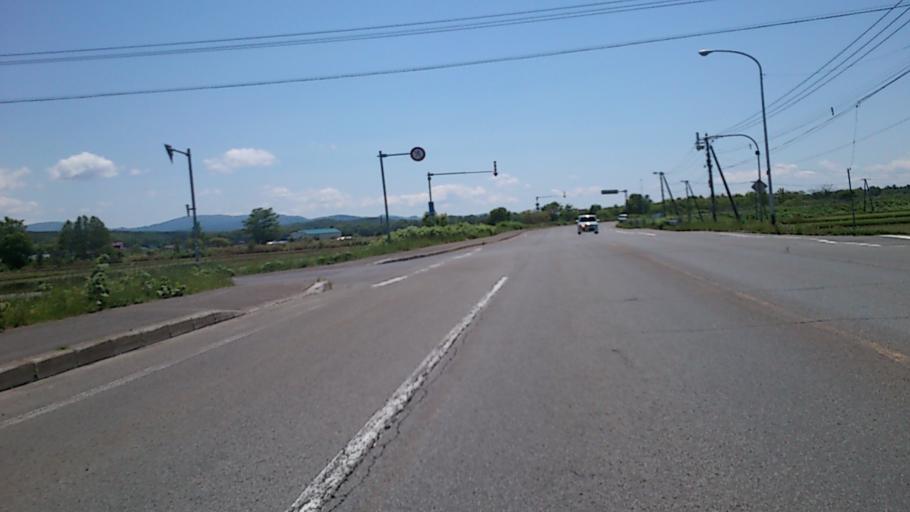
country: JP
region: Hokkaido
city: Nayoro
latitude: 44.3173
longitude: 142.4570
